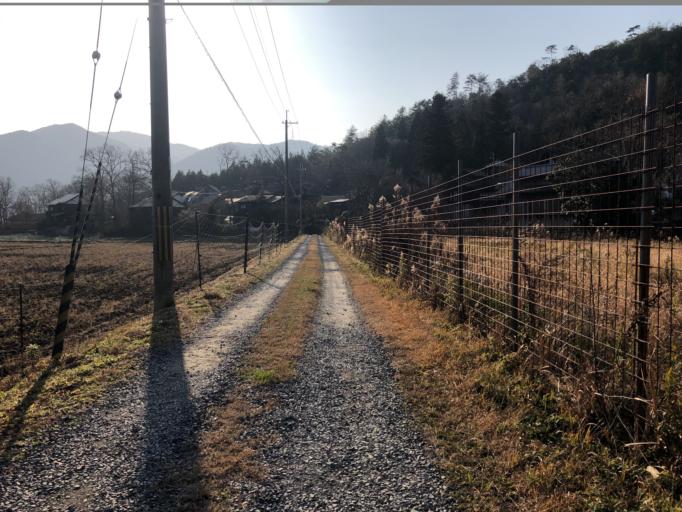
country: JP
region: Kyoto
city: Kameoka
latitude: 35.0580
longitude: 135.4771
